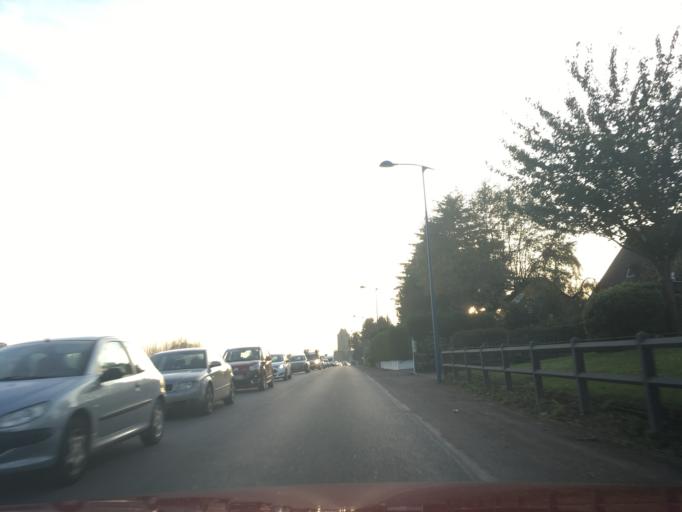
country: FR
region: Lower Normandy
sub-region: Departement de la Manche
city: Avranches
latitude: 48.7003
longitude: -1.3568
